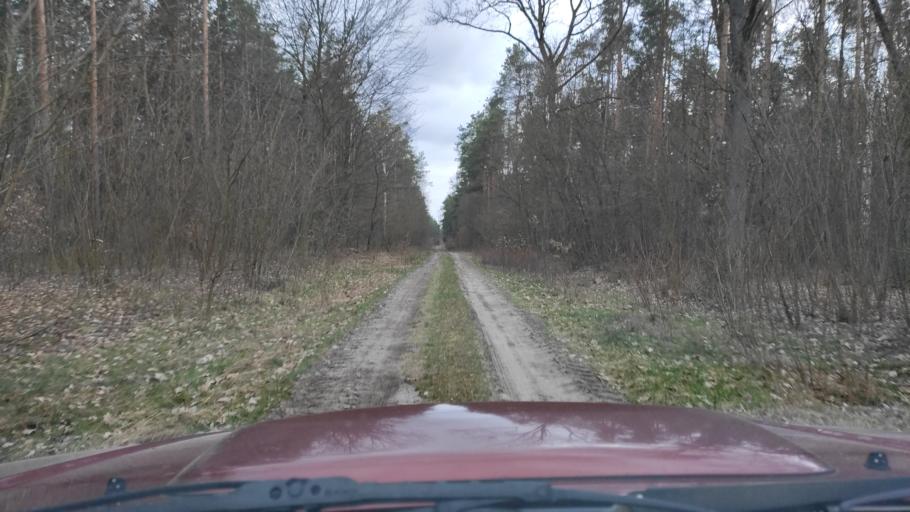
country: PL
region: Masovian Voivodeship
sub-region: Powiat kozienicki
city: Garbatka-Letnisko
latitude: 51.5063
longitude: 21.5553
